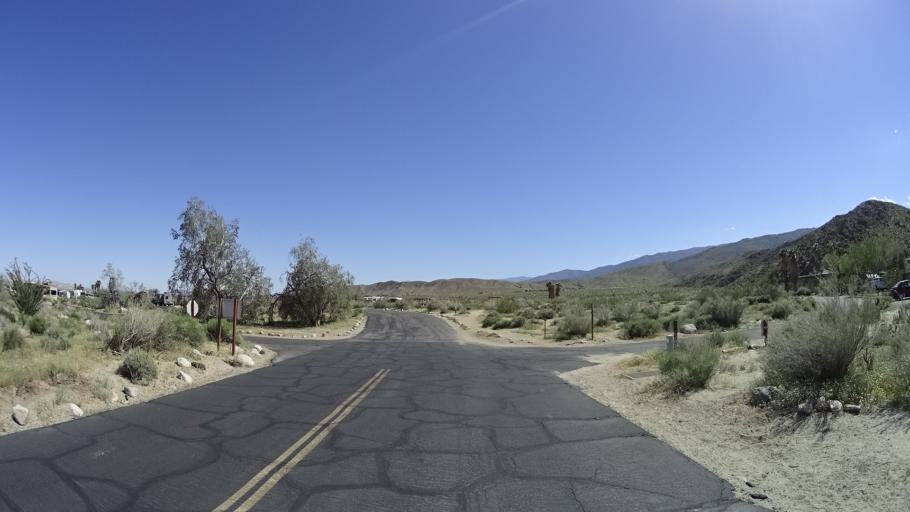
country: US
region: California
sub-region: San Diego County
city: Borrego Springs
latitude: 33.2692
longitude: -116.4101
